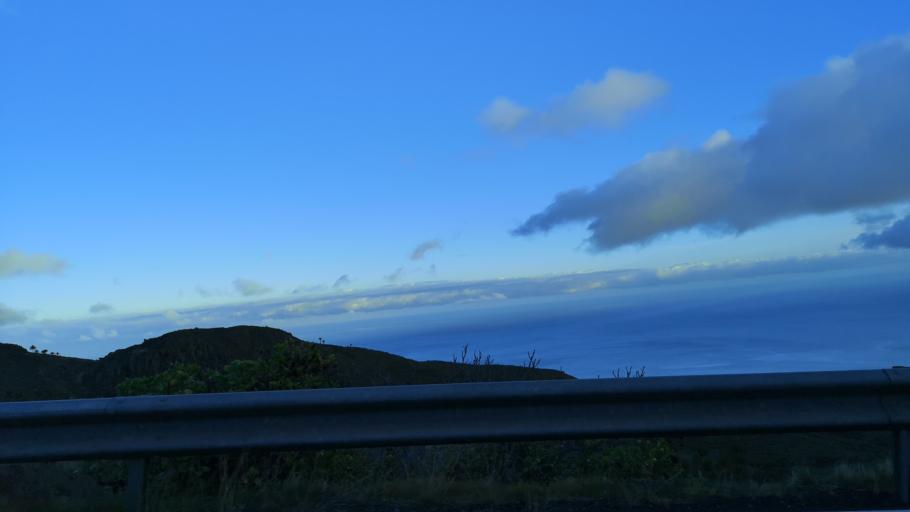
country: ES
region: Canary Islands
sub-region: Provincia de Santa Cruz de Tenerife
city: Alajero
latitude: 28.0531
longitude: -17.2319
